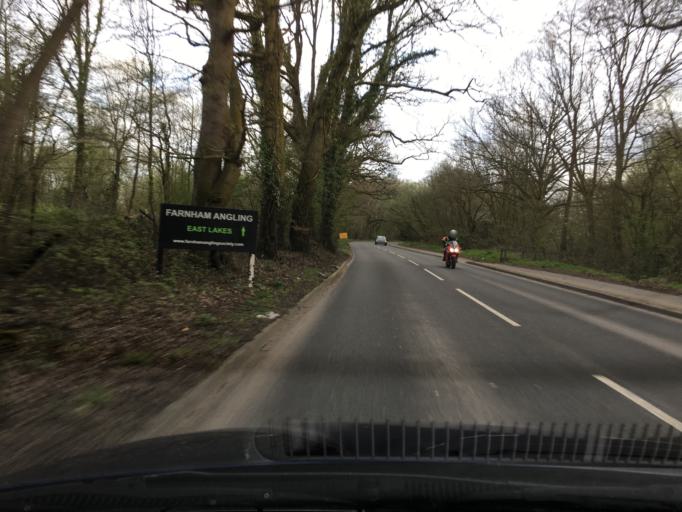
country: GB
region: England
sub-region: Hampshire
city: Yateley
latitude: 51.3453
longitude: -0.8163
